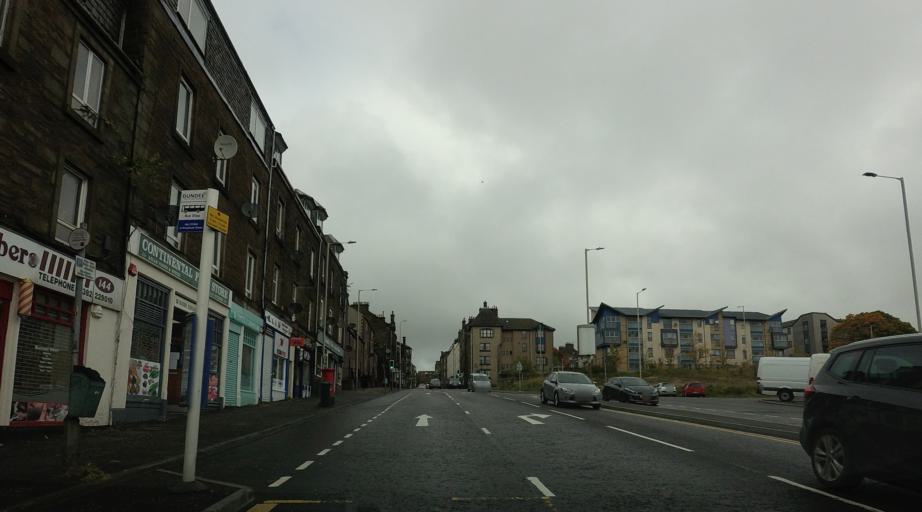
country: GB
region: Scotland
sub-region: Dundee City
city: Dundee
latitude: 56.4674
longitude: -2.9730
